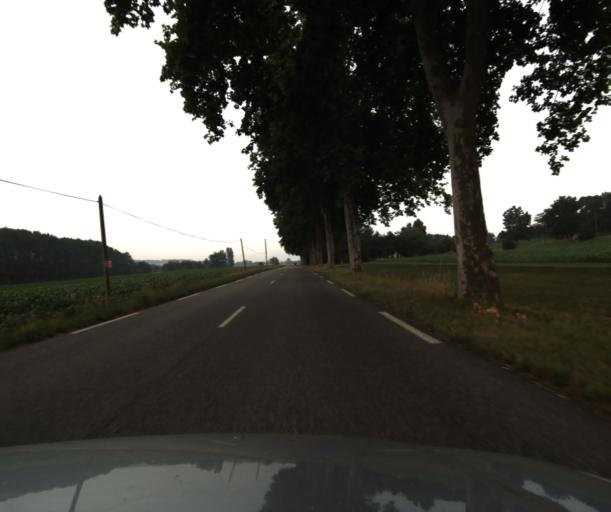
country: FR
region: Midi-Pyrenees
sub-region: Departement du Tarn-et-Garonne
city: Beaumont-de-Lomagne
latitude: 43.8352
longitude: 0.9245
